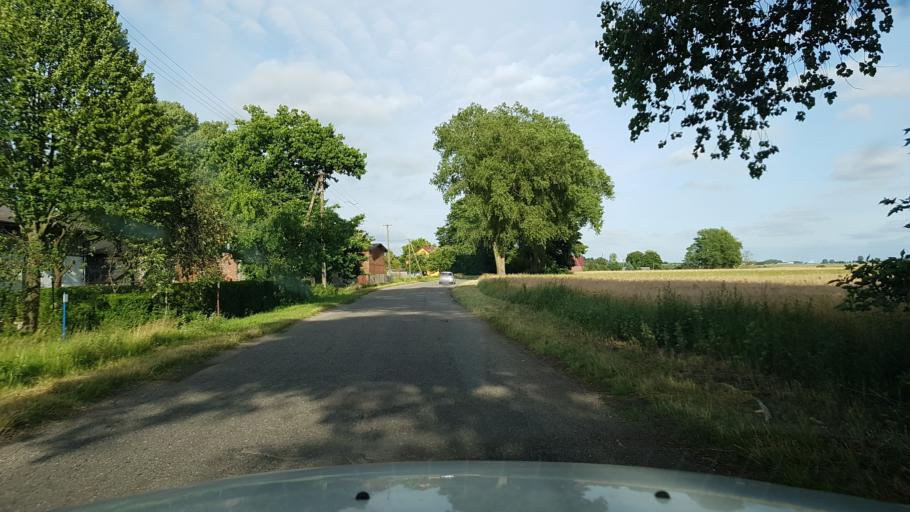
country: PL
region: West Pomeranian Voivodeship
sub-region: Powiat kolobrzeski
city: Grzybowo
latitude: 54.0915
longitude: 15.5438
